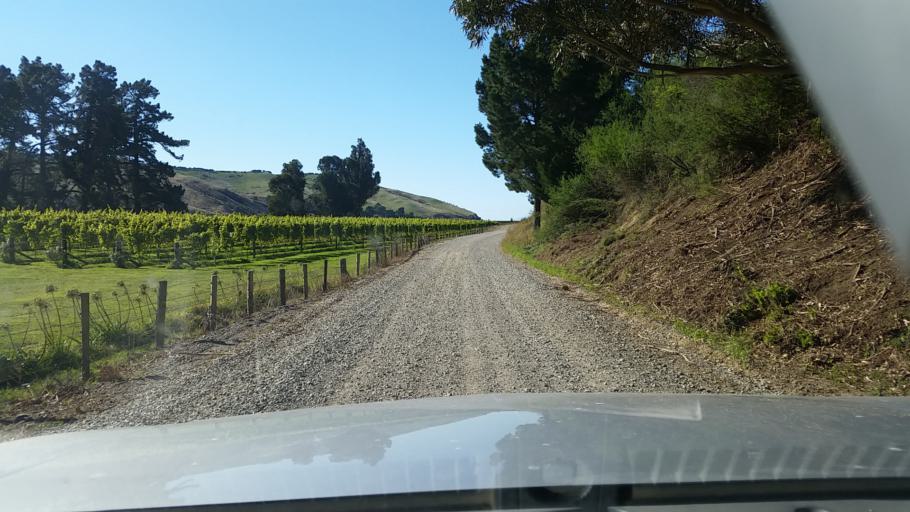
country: NZ
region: Marlborough
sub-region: Marlborough District
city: Blenheim
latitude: -41.6697
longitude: 174.1482
